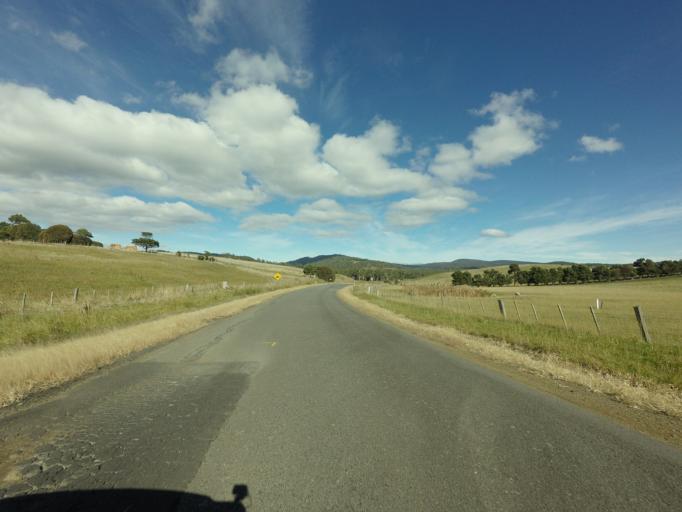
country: AU
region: Tasmania
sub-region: Clarence
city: Sandford
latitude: -43.0223
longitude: 147.7225
